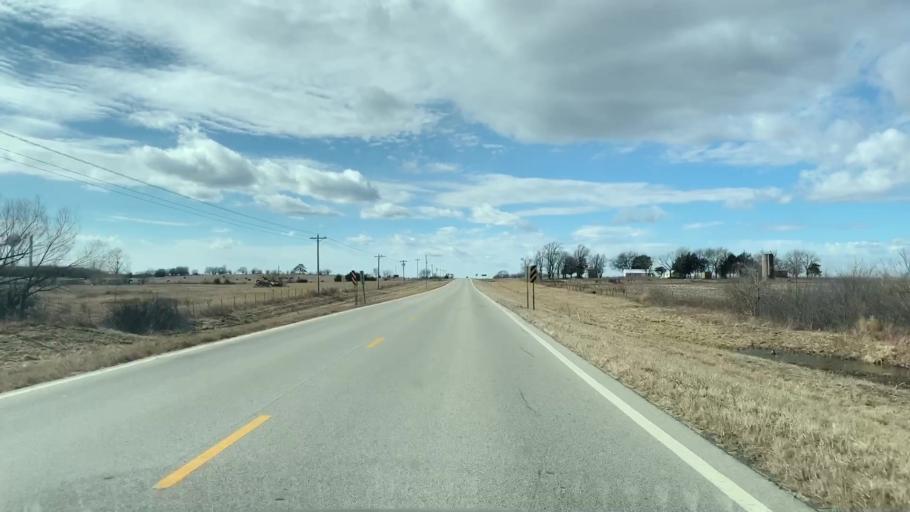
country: US
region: Kansas
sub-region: Neosho County
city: Erie
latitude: 37.5293
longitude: -95.3575
